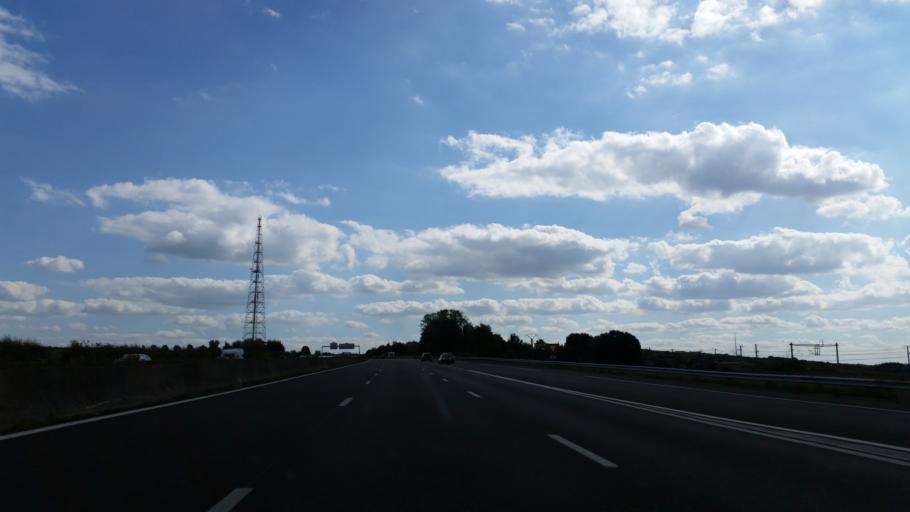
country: FR
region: Picardie
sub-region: Departement de la Somme
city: Moislains
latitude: 50.0134
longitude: 2.8792
